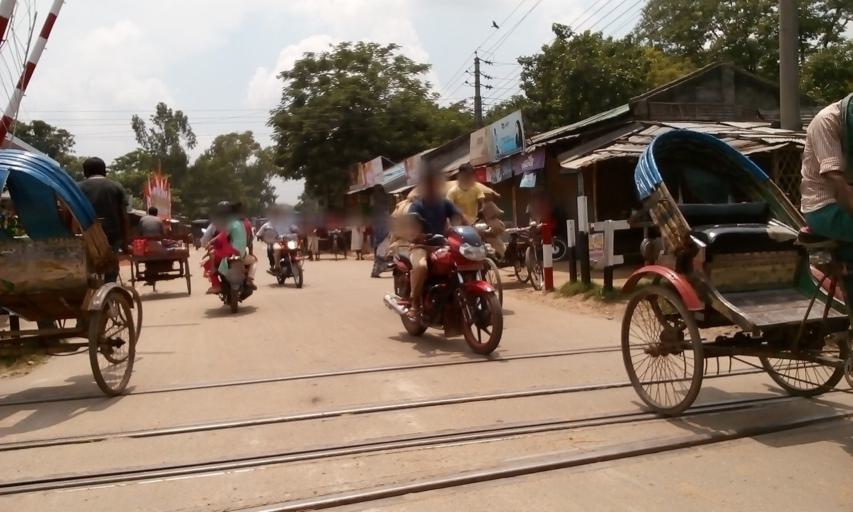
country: BD
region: Rangpur Division
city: Parbatipur
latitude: 25.4989
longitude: 88.9681
